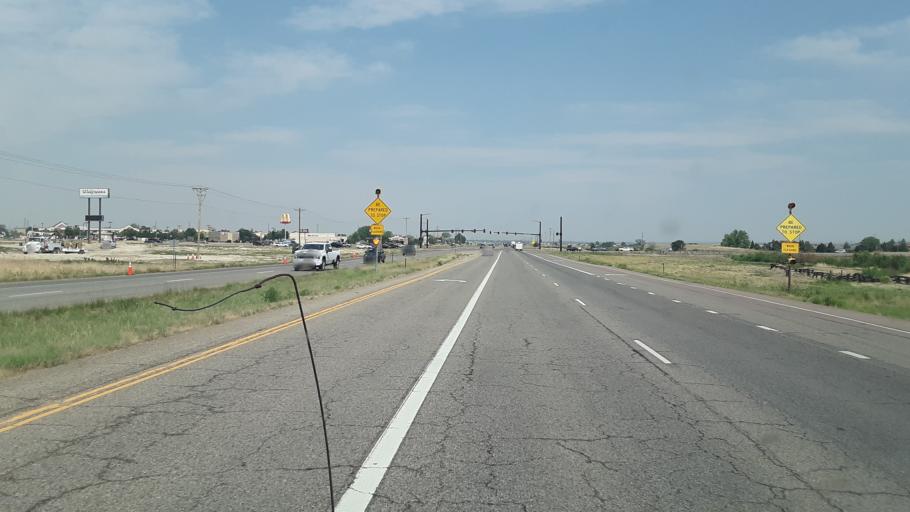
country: US
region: Colorado
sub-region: Pueblo County
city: Pueblo West
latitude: 38.3247
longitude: -104.7045
